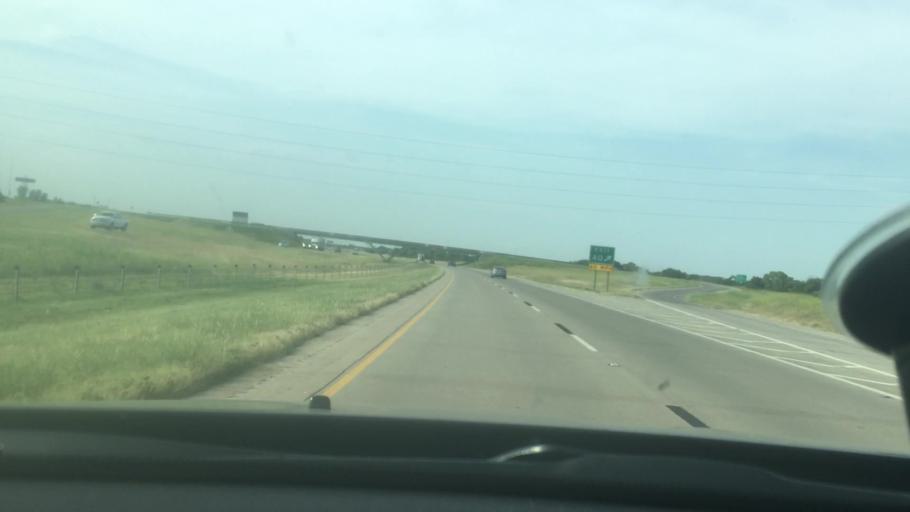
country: US
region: Oklahoma
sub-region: Carter County
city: Ardmore
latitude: 34.3068
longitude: -97.1597
